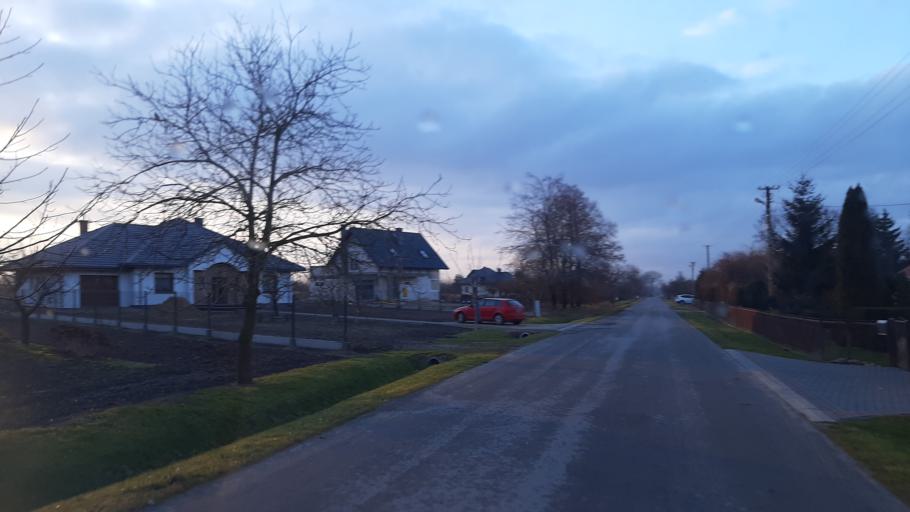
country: PL
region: Lublin Voivodeship
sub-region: Powiat lubelski
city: Garbow
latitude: 51.3801
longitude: 22.4002
